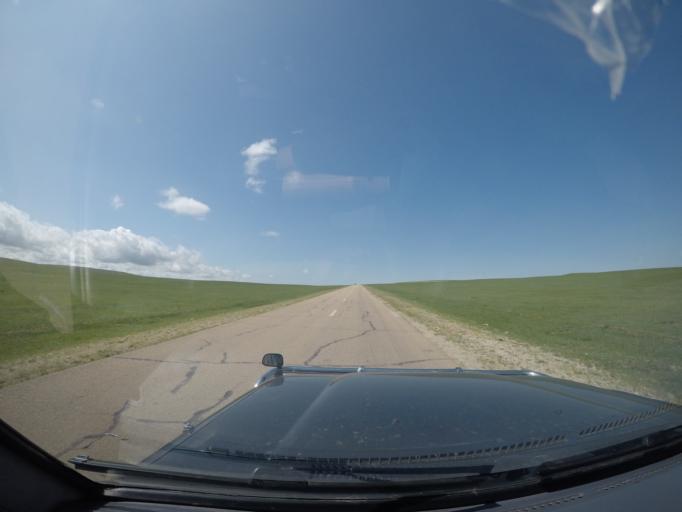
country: MN
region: Hentiy
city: Bayan
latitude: 47.2845
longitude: 110.9759
